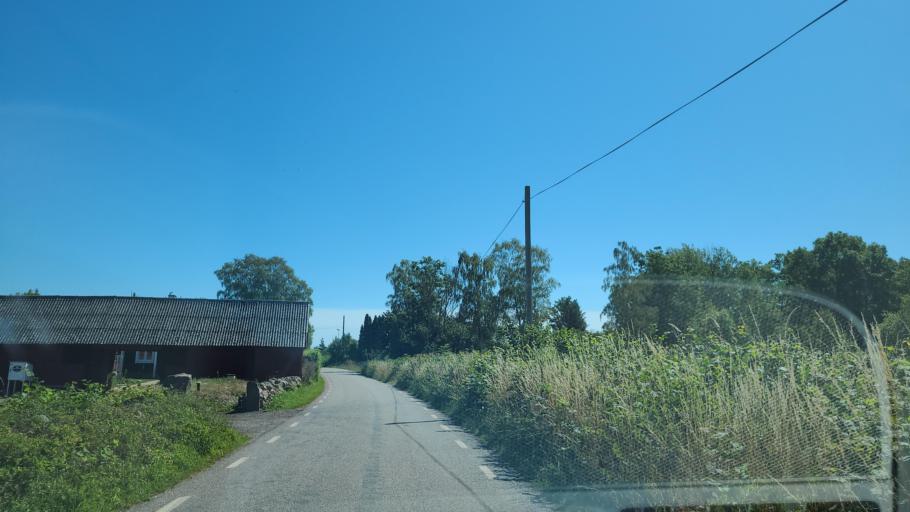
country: SE
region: Kalmar
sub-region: Borgholms Kommun
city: Borgholm
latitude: 56.7674
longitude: 16.6384
